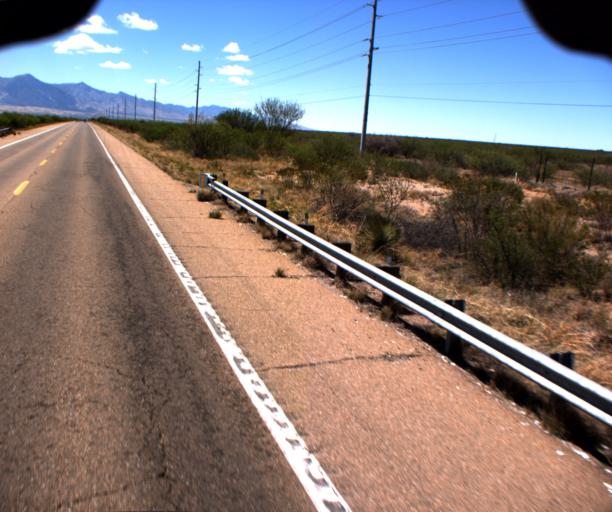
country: US
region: Arizona
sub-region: Cochise County
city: Naco
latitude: 31.3764
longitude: -110.0110
